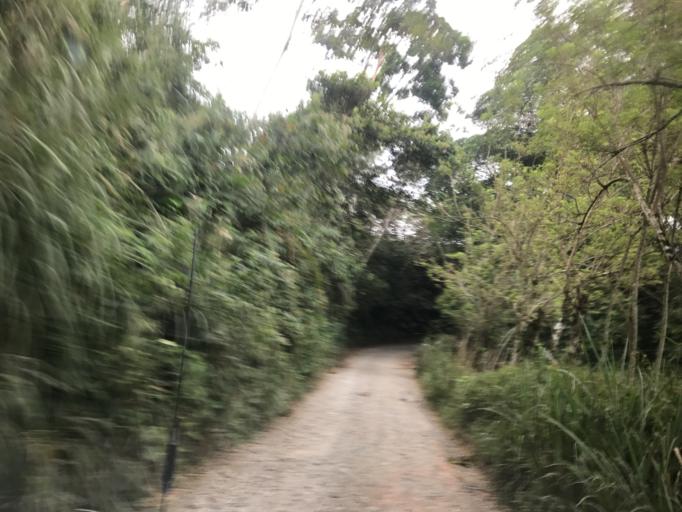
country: CO
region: Valle del Cauca
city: Obando
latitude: 4.5530
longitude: -75.8676
